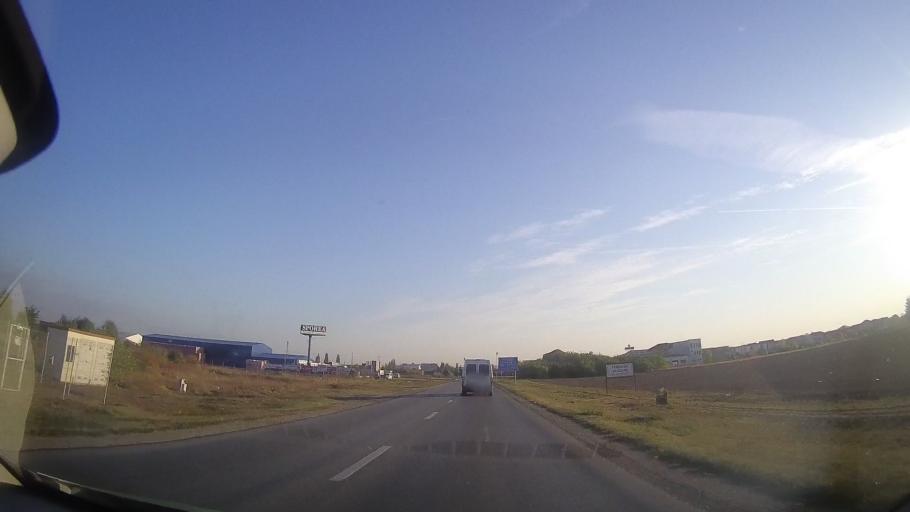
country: RO
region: Timis
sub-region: Comuna Dumbravita
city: Dumbravita
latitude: 45.8099
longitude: 21.2586
